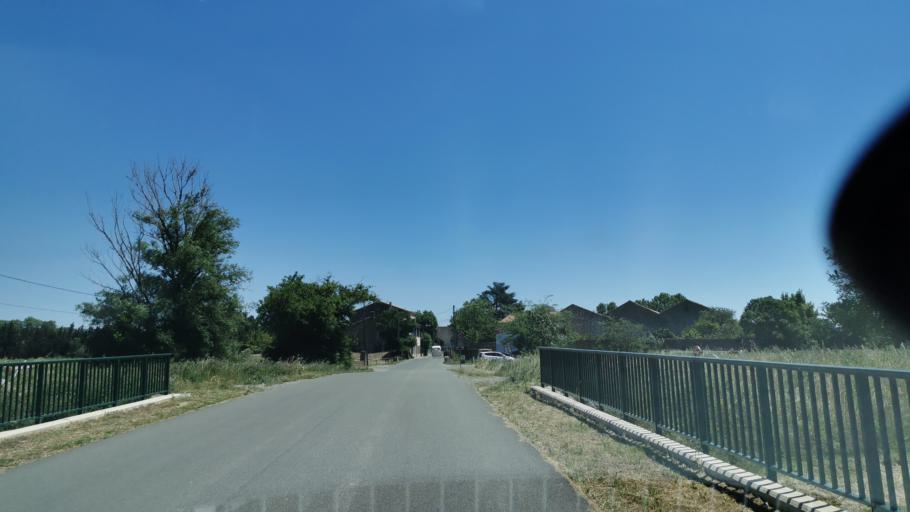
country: FR
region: Languedoc-Roussillon
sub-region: Departement de l'Aude
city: Saint-Marcel-sur-Aude
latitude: 43.2571
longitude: 2.9411
